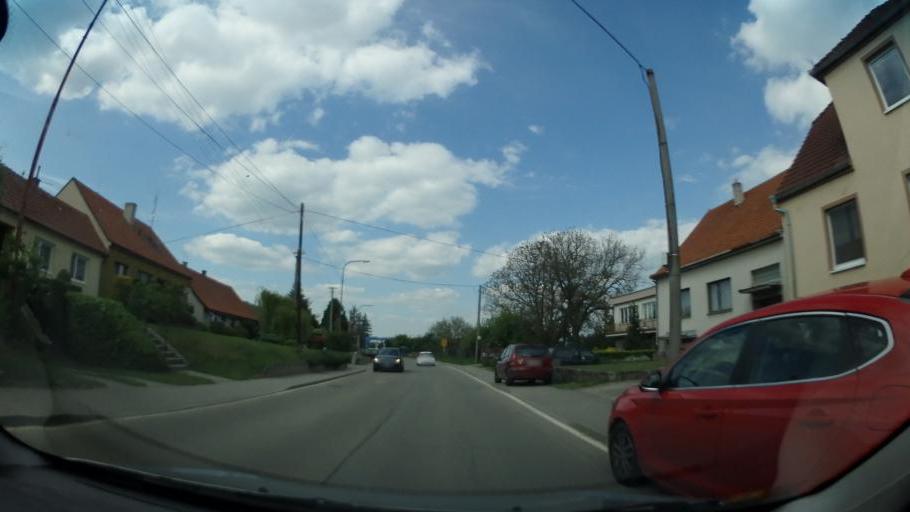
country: CZ
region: Vysocina
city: Mohelno
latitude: 49.1177
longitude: 16.1957
